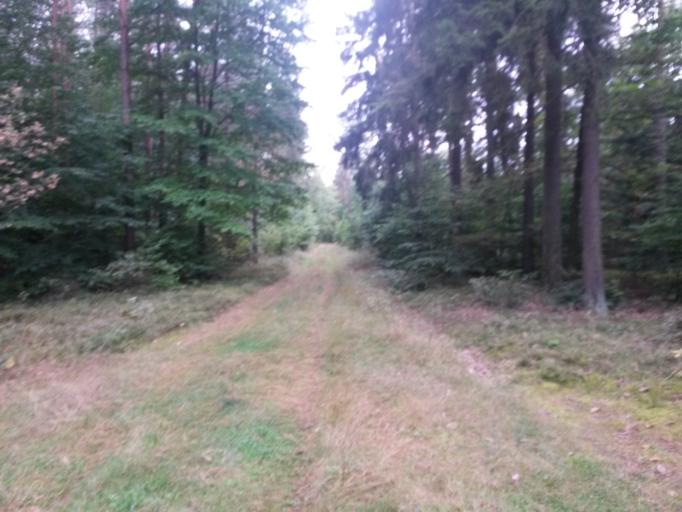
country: PL
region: Warmian-Masurian Voivodeship
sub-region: Powiat nowomiejski
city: Biskupiec
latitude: 53.5073
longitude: 19.4705
